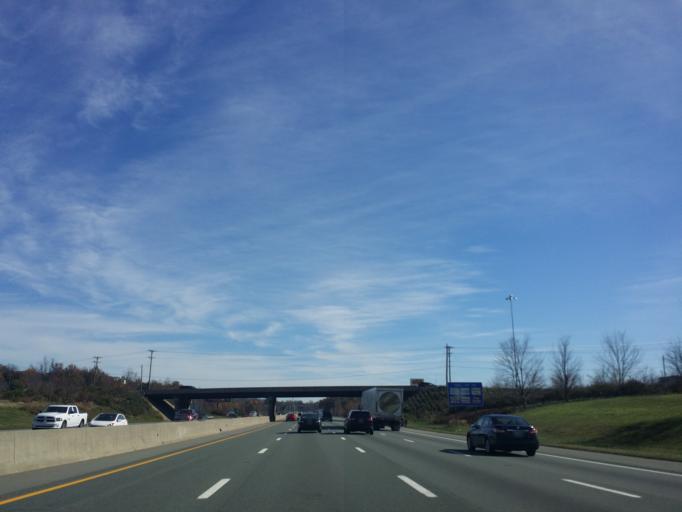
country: US
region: North Carolina
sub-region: Alamance County
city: Mebane
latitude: 36.0686
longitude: -79.3002
